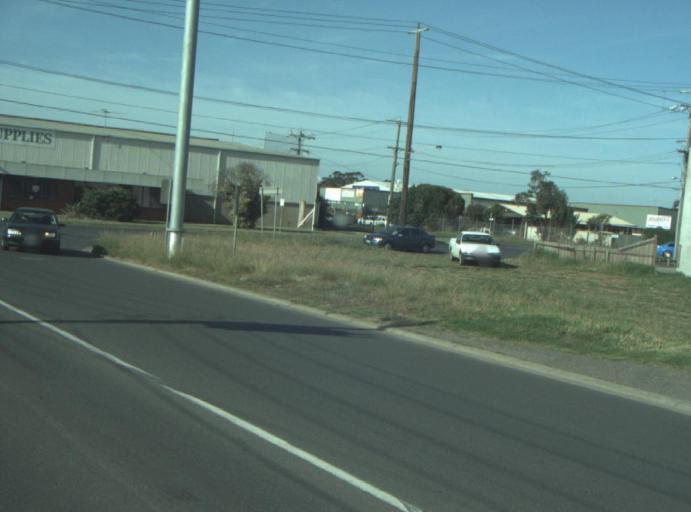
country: AU
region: Victoria
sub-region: Greater Geelong
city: Geelong West
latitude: -38.1221
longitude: 144.3478
